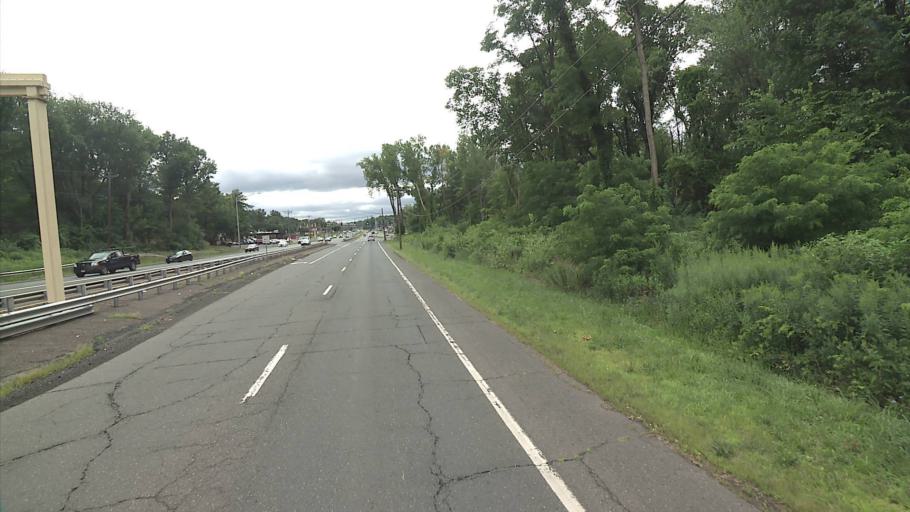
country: US
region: Connecticut
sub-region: Hartford County
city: Newington
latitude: 41.7112
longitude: -72.6990
